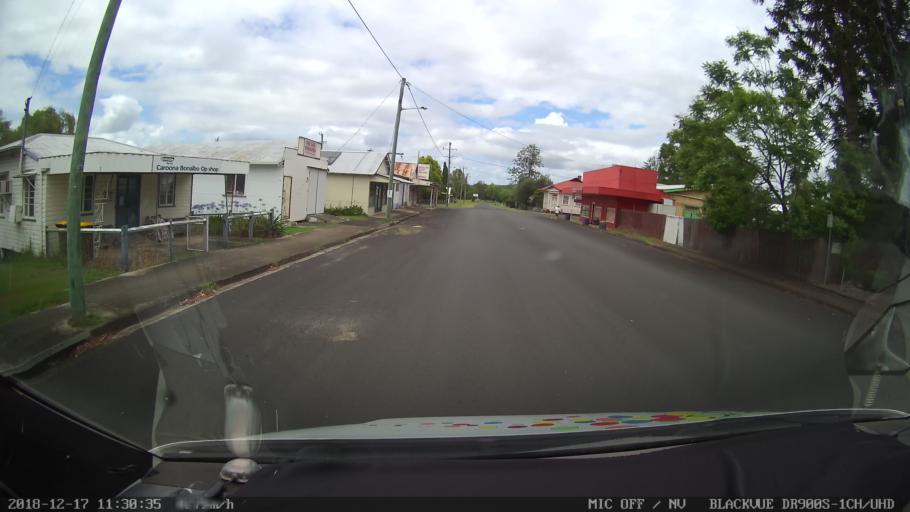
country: AU
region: New South Wales
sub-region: Kyogle
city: Kyogle
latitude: -28.7374
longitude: 152.6232
